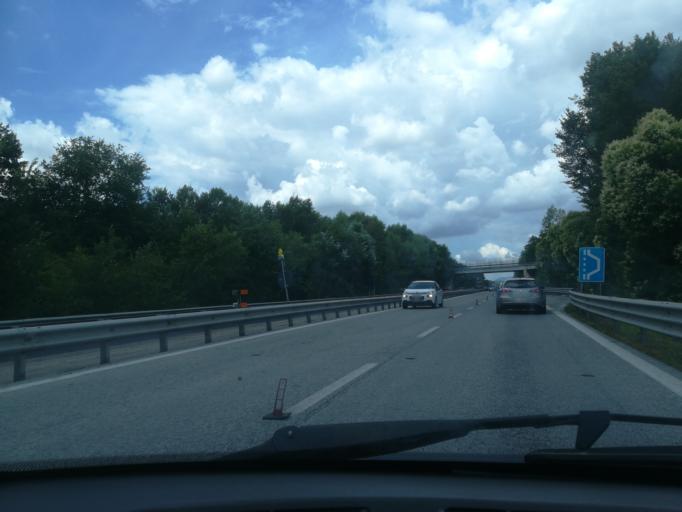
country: IT
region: The Marches
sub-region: Provincia di Macerata
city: Corridonia
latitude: 43.2689
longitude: 13.5138
